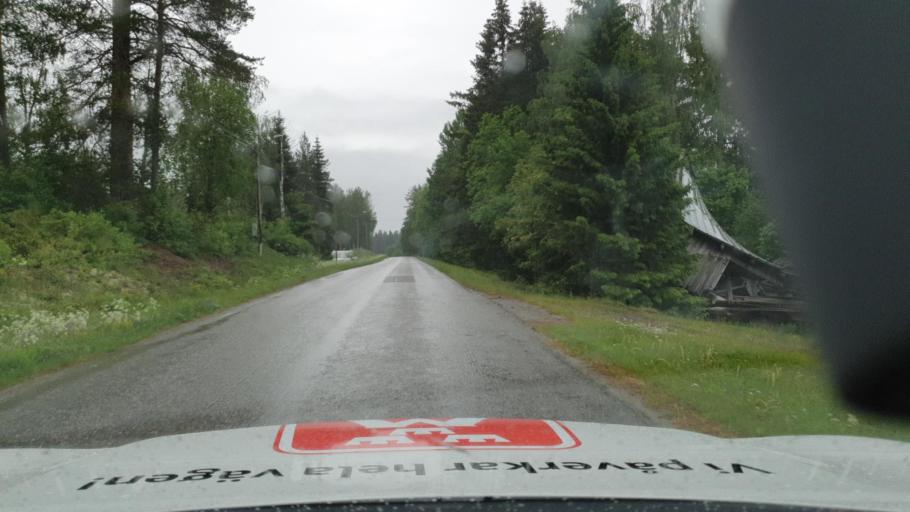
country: SE
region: Vaesterbotten
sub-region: Nordmalings Kommun
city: Nordmaling
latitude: 63.8017
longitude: 19.5045
